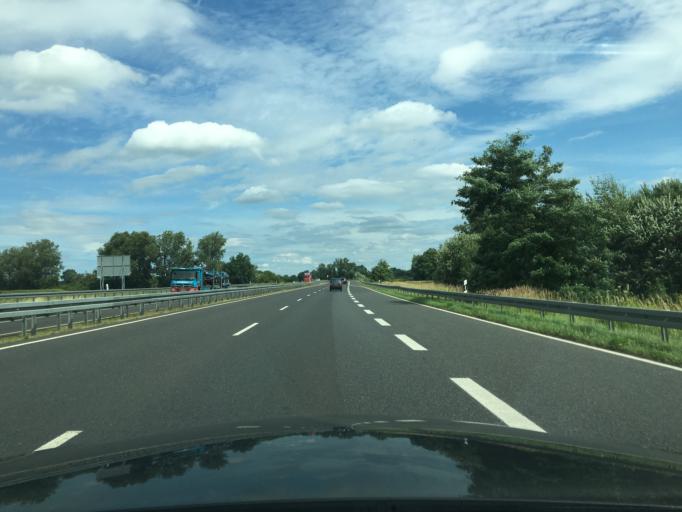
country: DE
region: Brandenburg
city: Leegebruch
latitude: 52.7531
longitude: 13.1982
